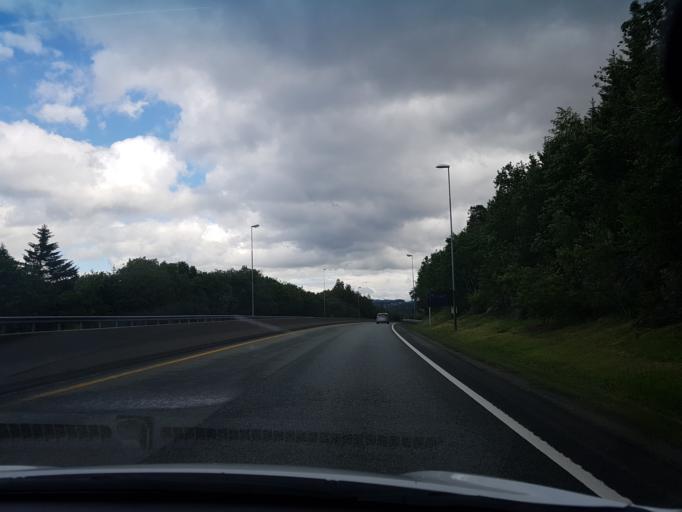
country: NO
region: Sor-Trondelag
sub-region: Malvik
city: Malvik
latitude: 63.4266
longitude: 10.6543
